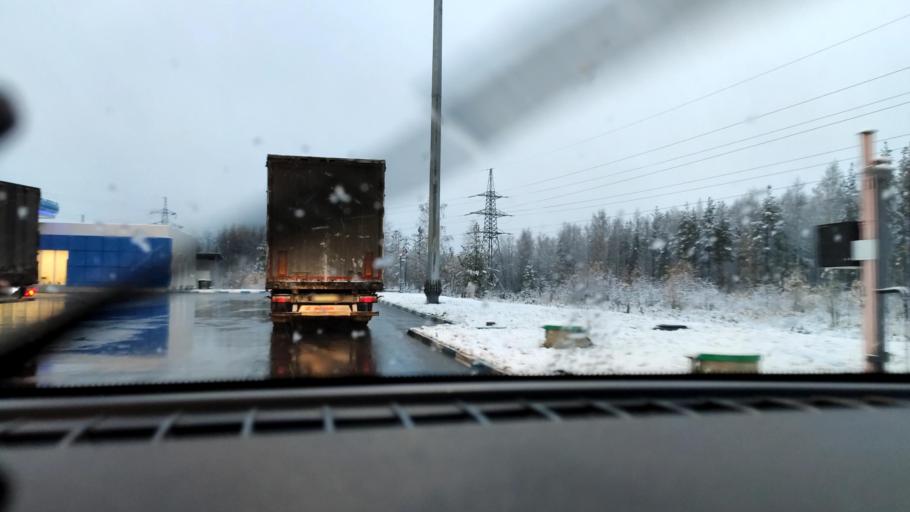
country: RU
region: Perm
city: Overyata
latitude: 58.0165
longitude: 55.8942
